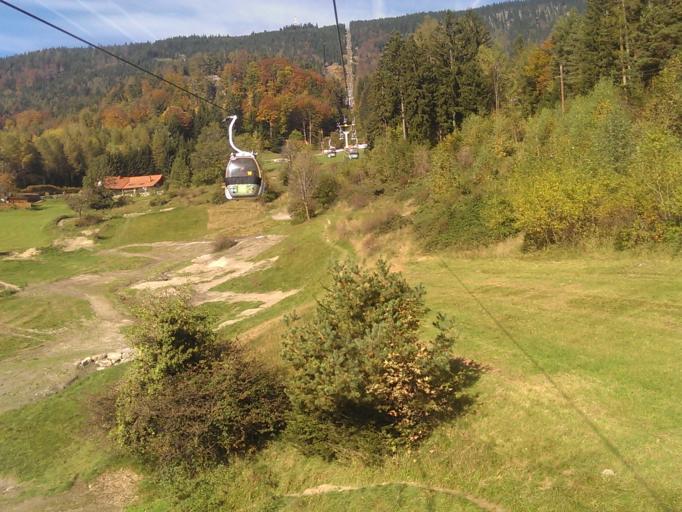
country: AT
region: Styria
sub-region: Politischer Bezirk Graz-Umgebung
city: Sankt Radegund bei Graz
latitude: 47.1868
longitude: 15.4845
